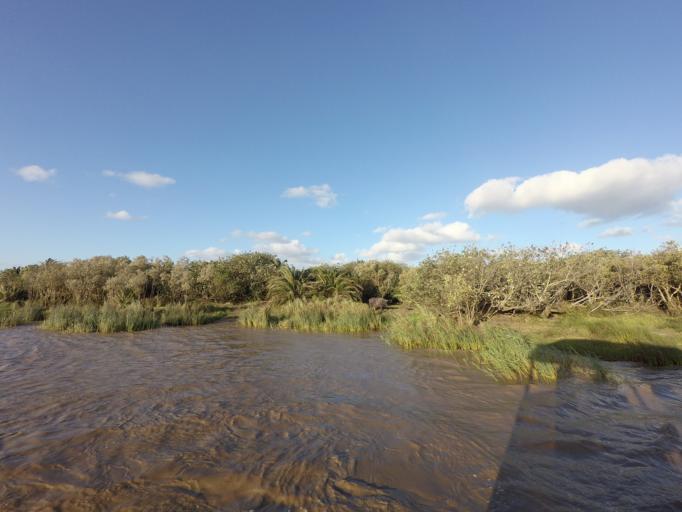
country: ZA
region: KwaZulu-Natal
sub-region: uMkhanyakude District Municipality
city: Mtubatuba
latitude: -28.3467
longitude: 32.4110
